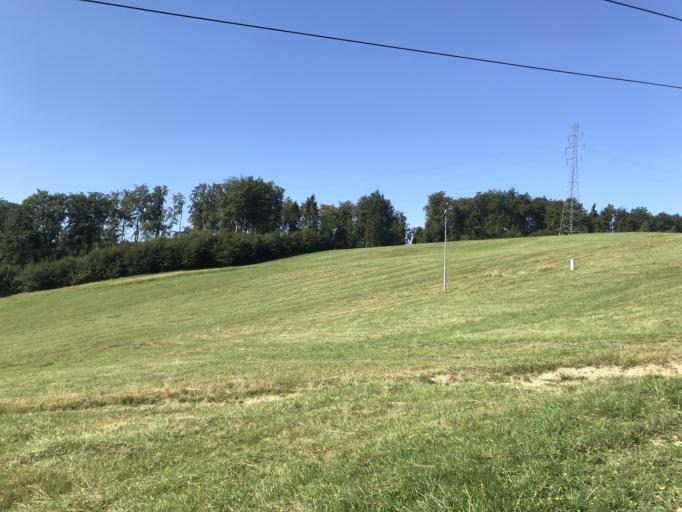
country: PL
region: Lesser Poland Voivodeship
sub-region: Powiat nowosadecki
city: Muszyna
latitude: 49.3998
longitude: 20.8489
